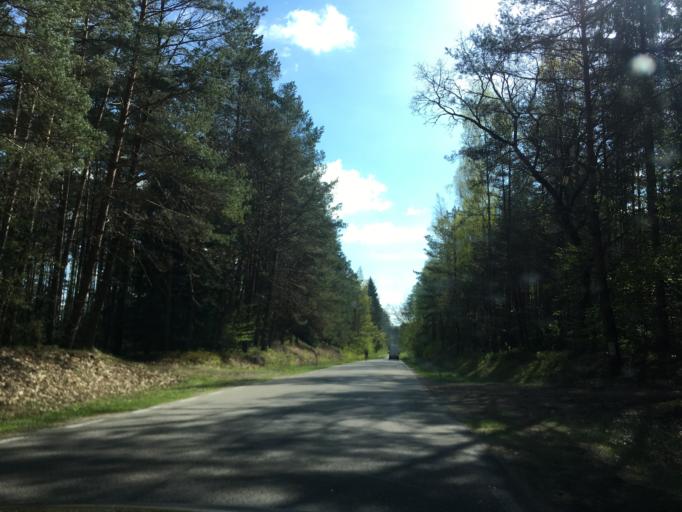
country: PL
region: Warmian-Masurian Voivodeship
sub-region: Powiat piski
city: Ruciane-Nida
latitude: 53.6778
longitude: 21.5980
